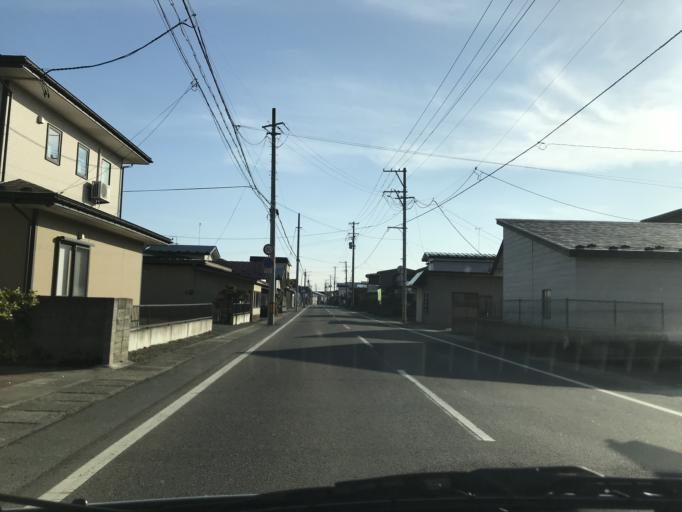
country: JP
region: Iwate
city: Kitakami
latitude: 39.2615
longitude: 141.1144
